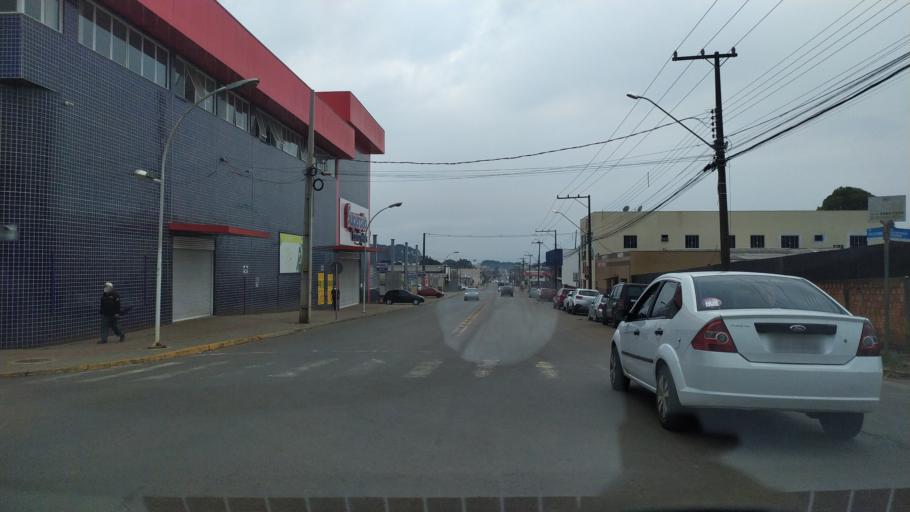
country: BR
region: Parana
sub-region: Palmas
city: Palmas
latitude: -26.4904
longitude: -51.9985
